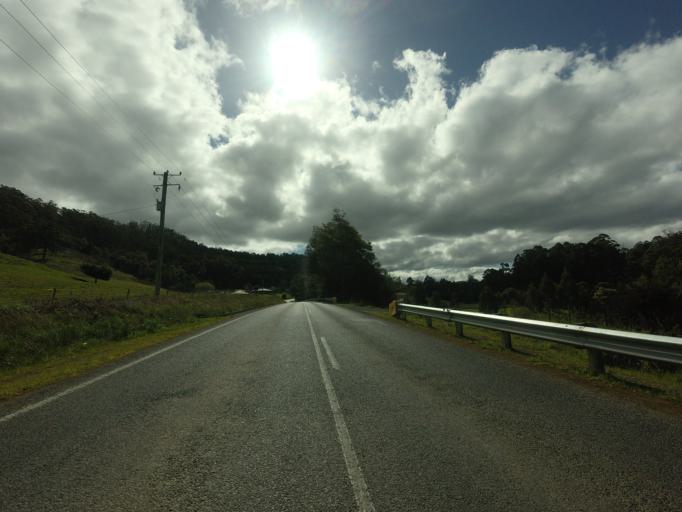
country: AU
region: Tasmania
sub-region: Huon Valley
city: Geeveston
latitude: -43.3052
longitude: 147.0088
